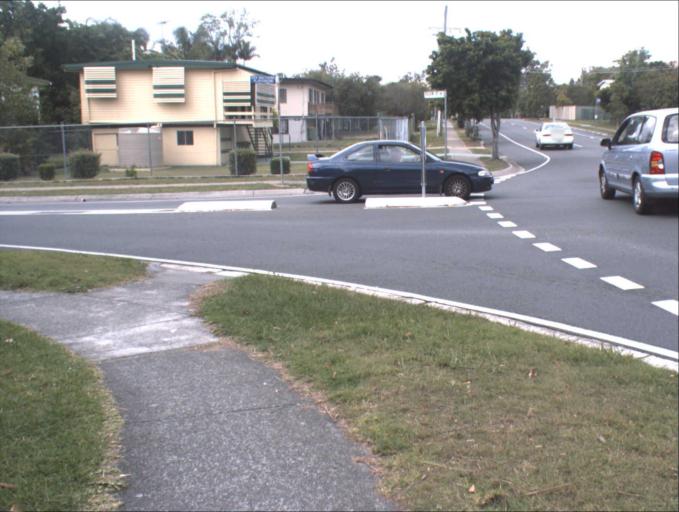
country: AU
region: Queensland
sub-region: Logan
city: Logan City
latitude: -27.6451
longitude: 153.1093
